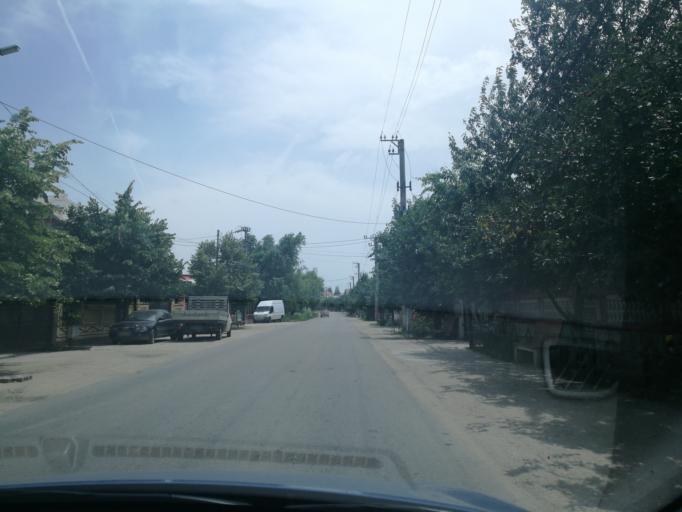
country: RO
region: Ilfov
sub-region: Comuna Jilava
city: Jilava
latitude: 44.3194
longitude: 26.1014
